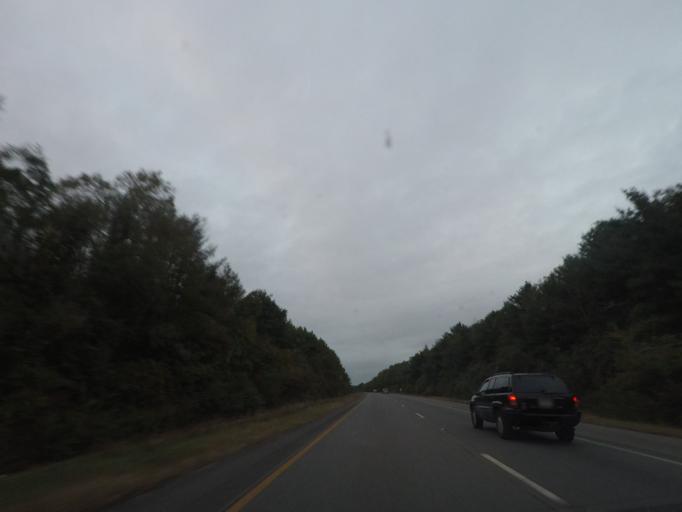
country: US
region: Massachusetts
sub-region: Worcester County
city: Oxford
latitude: 42.0984
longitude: -71.8594
